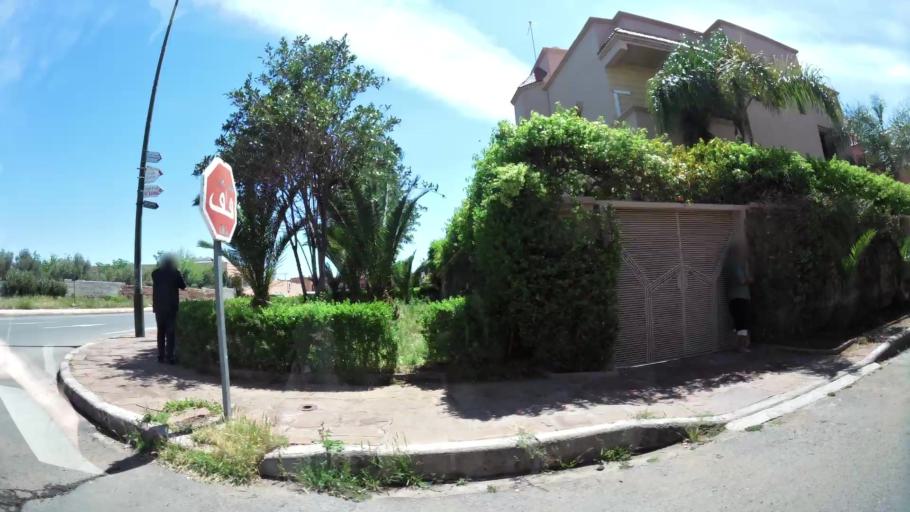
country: MA
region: Marrakech-Tensift-Al Haouz
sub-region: Marrakech
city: Marrakesh
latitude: 31.6402
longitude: -8.0606
